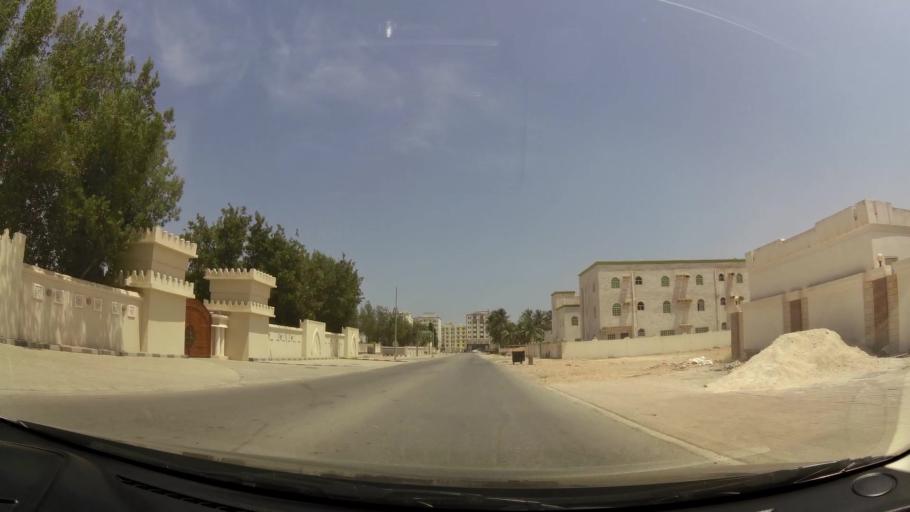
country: OM
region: Zufar
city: Salalah
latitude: 17.0559
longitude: 54.1547
